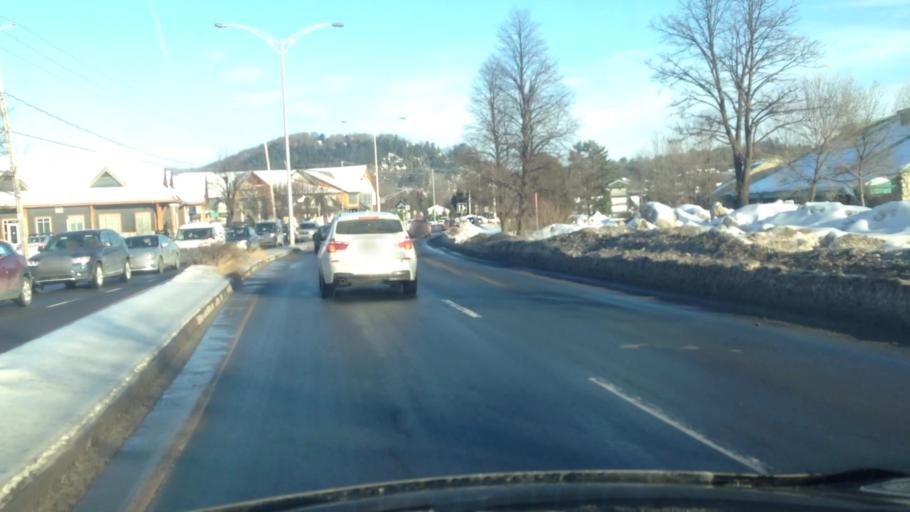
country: CA
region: Quebec
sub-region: Laurentides
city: Saint-Sauveur
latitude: 45.8918
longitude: -74.1566
